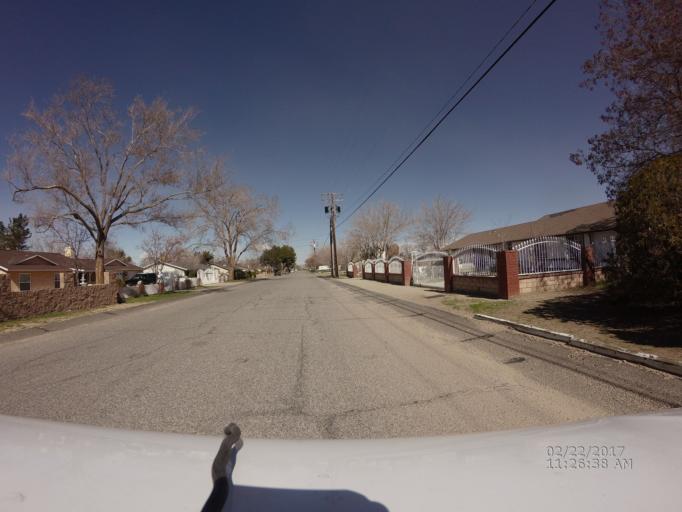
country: US
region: California
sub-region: Los Angeles County
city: Lake Los Angeles
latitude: 34.6198
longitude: -117.8149
